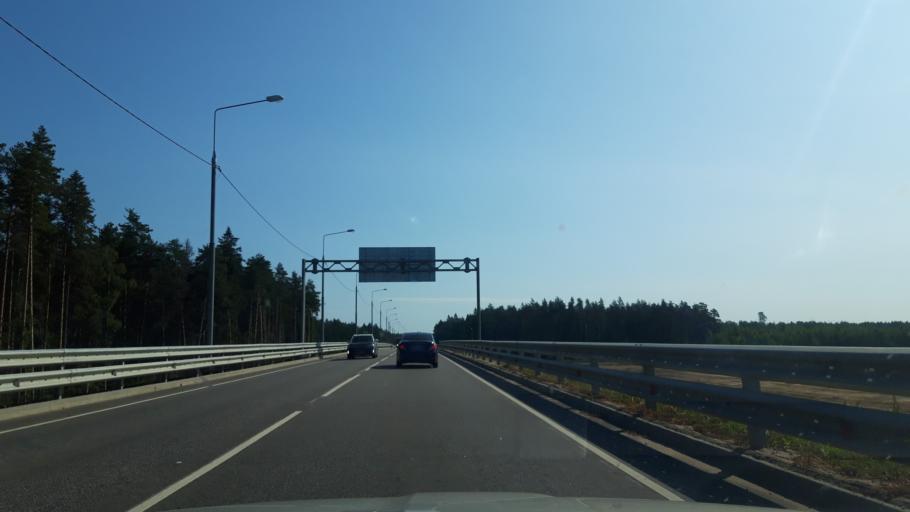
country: RU
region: Tverskaya
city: Novozavidovskiy
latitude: 56.5748
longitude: 36.4708
